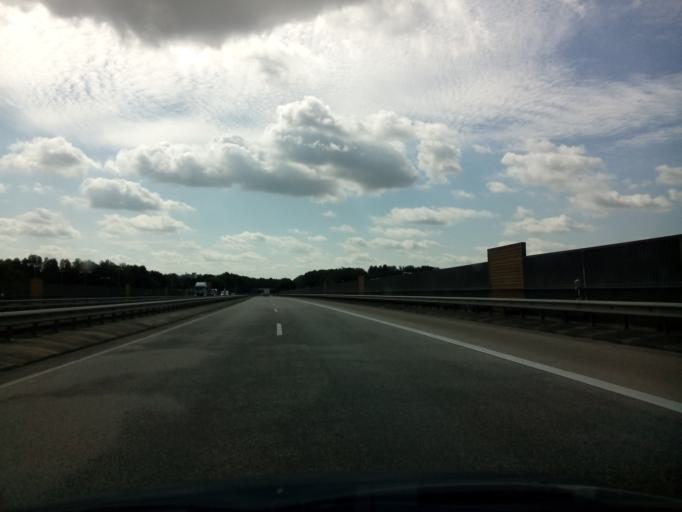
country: DE
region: Lower Saxony
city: Ritterhude
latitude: 53.1808
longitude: 8.7089
